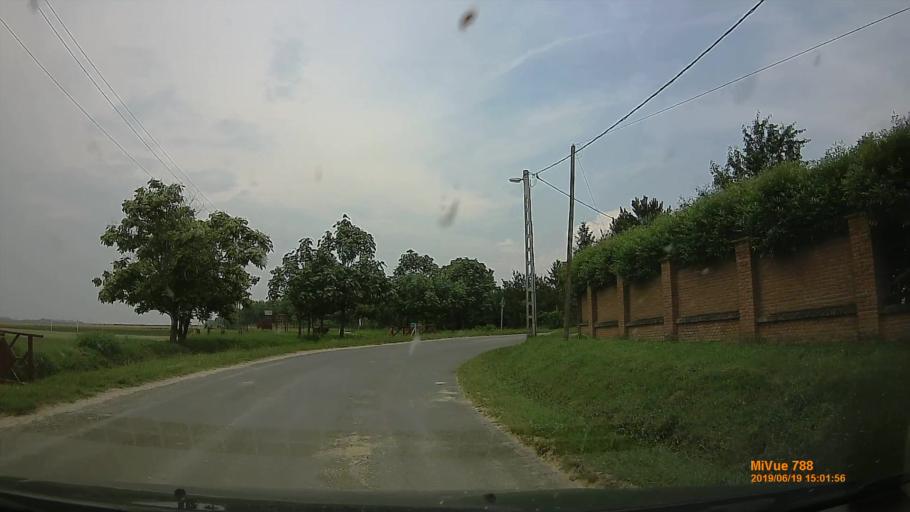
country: HU
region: Baranya
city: Szigetvar
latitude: 46.0897
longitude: 17.7982
